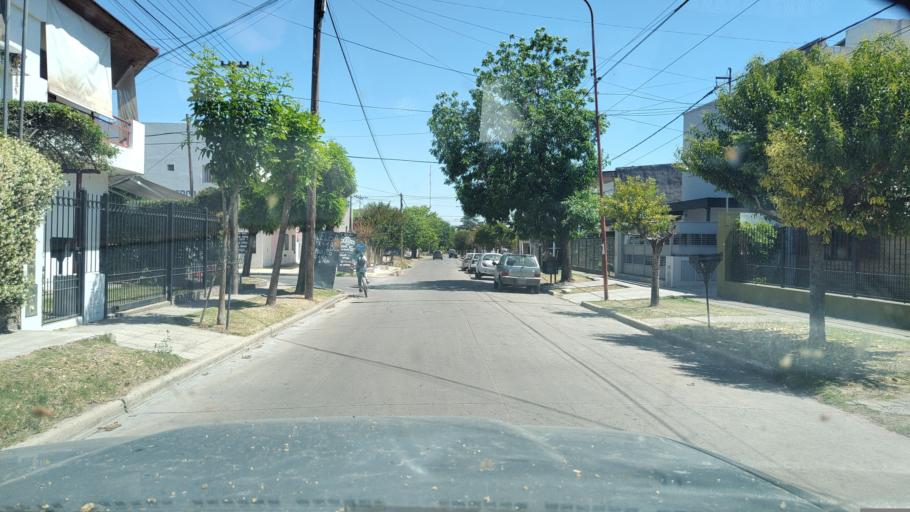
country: AR
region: Buenos Aires
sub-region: Partido de Lujan
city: Lujan
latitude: -34.5817
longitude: -59.1107
